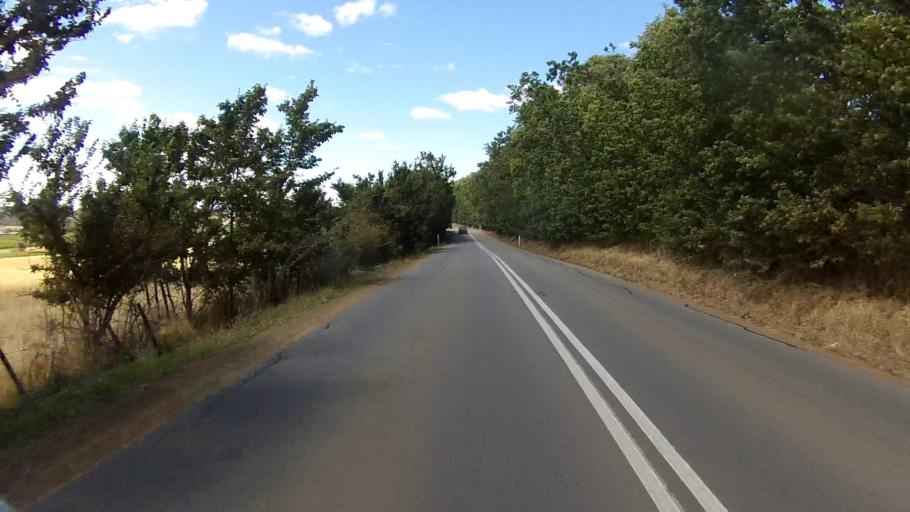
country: AU
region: Tasmania
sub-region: Clarence
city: Cambridge
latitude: -42.8059
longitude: 147.4236
